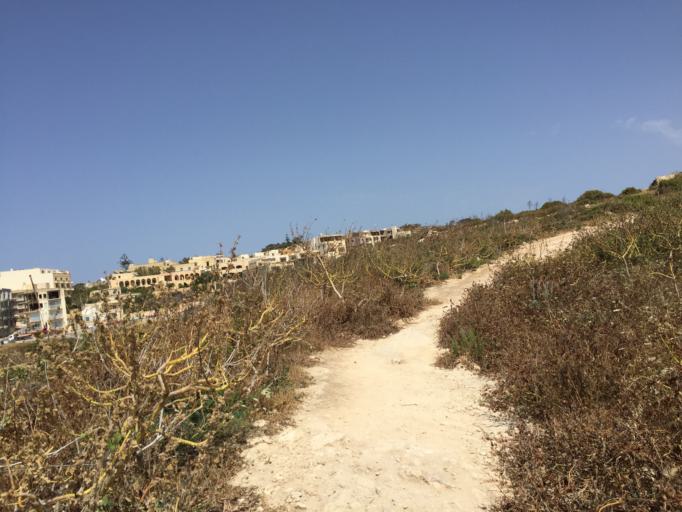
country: MT
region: Saint Lucia
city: Saint Lucia
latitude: 36.0276
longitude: 14.2138
